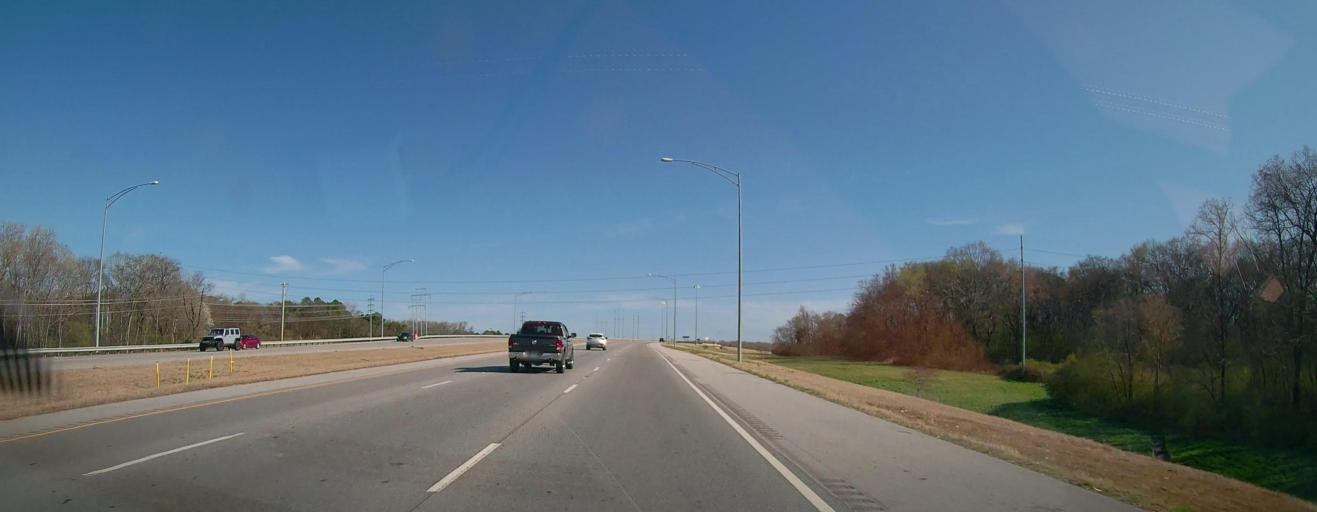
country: US
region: Alabama
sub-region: Lauderdale County
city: East Florence
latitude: 34.7862
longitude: -87.6379
